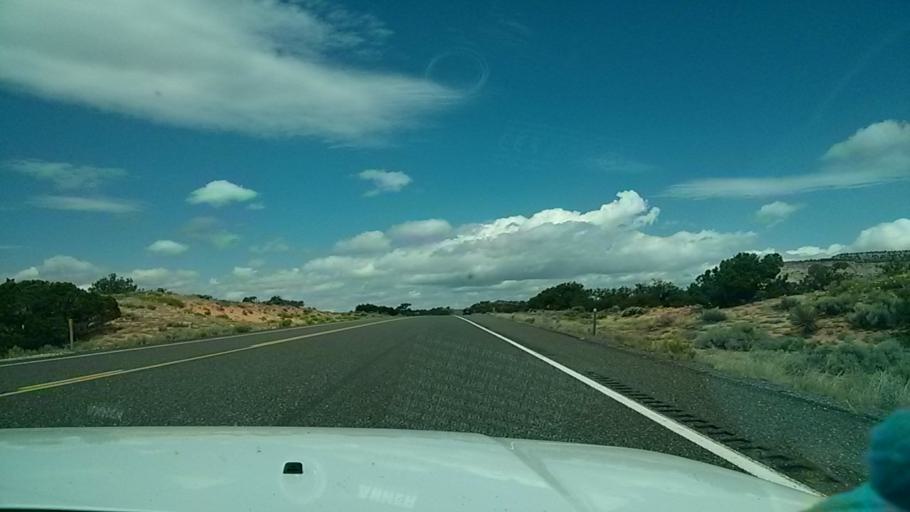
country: US
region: Utah
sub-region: Kane County
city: Kanab
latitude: 37.1669
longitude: -112.6031
